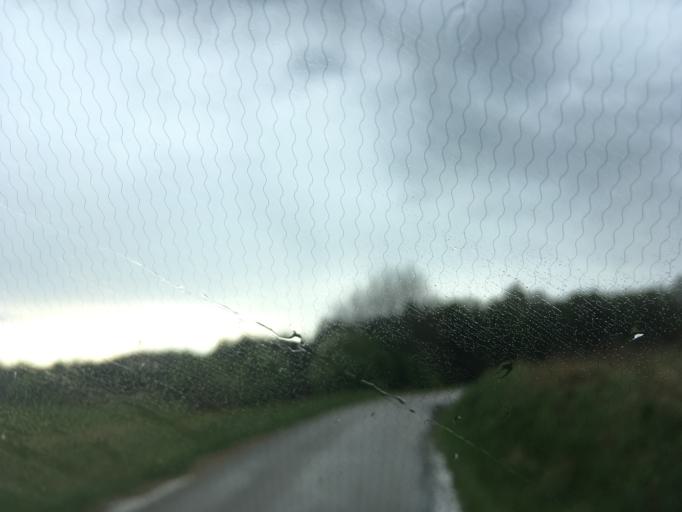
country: PL
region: Warmian-Masurian Voivodeship
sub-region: Powiat dzialdowski
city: Rybno
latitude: 53.3770
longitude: 19.9949
